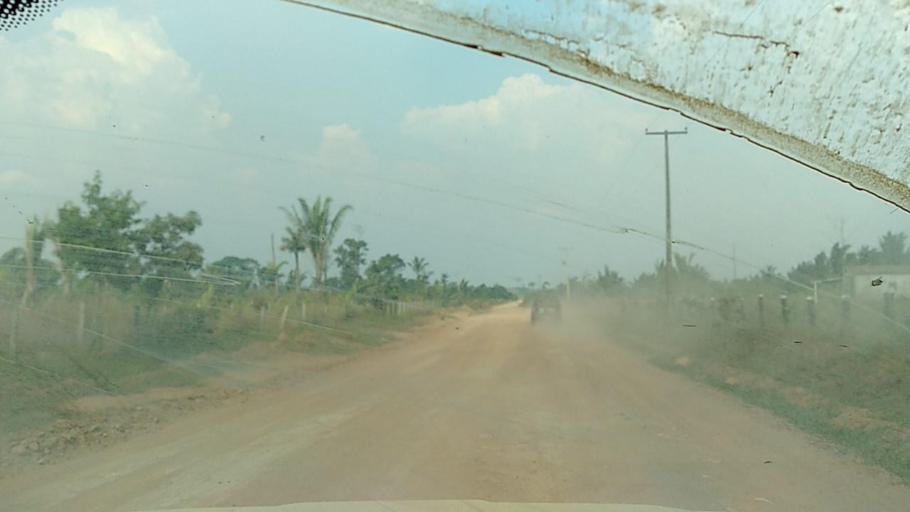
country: BR
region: Rondonia
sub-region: Porto Velho
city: Porto Velho
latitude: -8.6832
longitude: -63.1967
